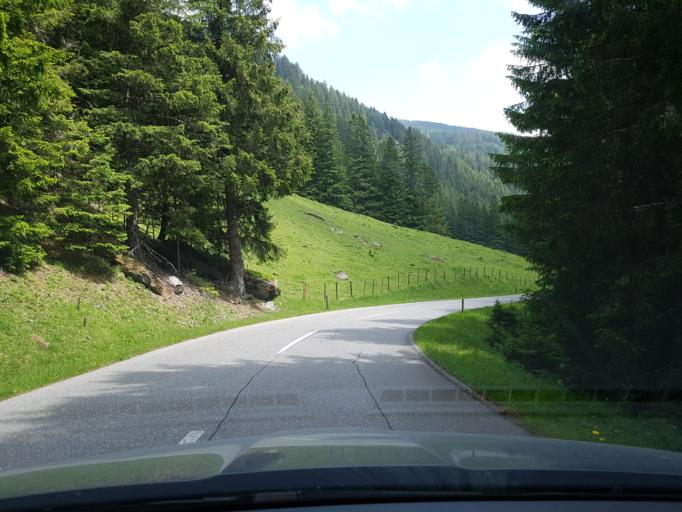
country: AT
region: Carinthia
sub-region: Politischer Bezirk Spittal an der Drau
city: Kleinkirchheim
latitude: 46.8910
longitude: 13.8322
